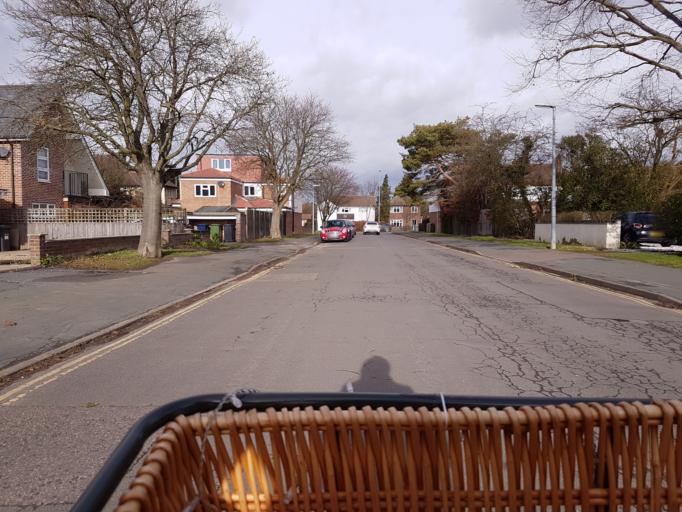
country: GB
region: England
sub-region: Cambridgeshire
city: Cambridge
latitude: 52.1786
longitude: 0.1513
